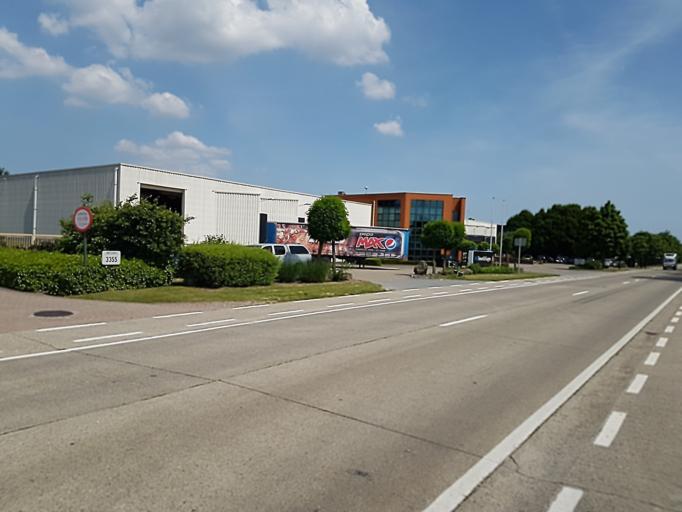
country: BE
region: Flanders
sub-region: Provincie Antwerpen
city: Westerlo
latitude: 51.1475
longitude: 4.9185
